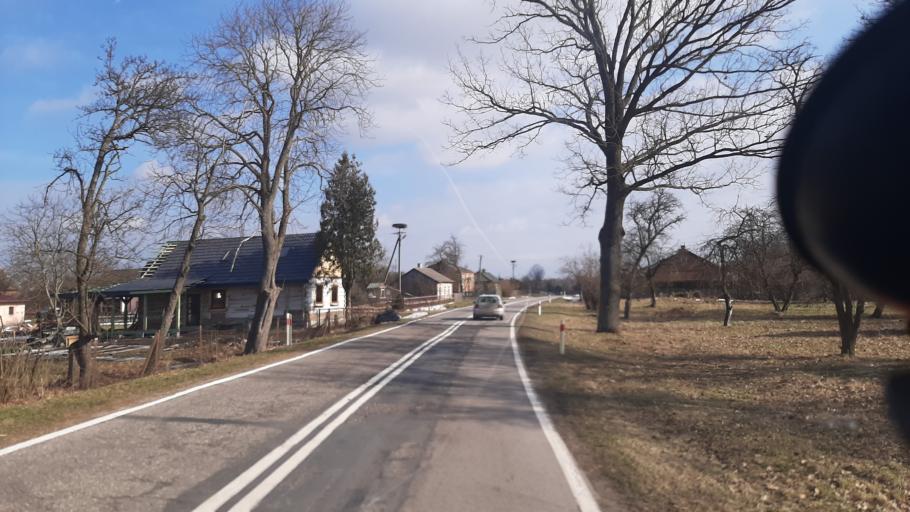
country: PL
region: Lublin Voivodeship
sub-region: Powiat parczewski
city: Sosnowica
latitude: 51.4975
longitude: 23.1676
